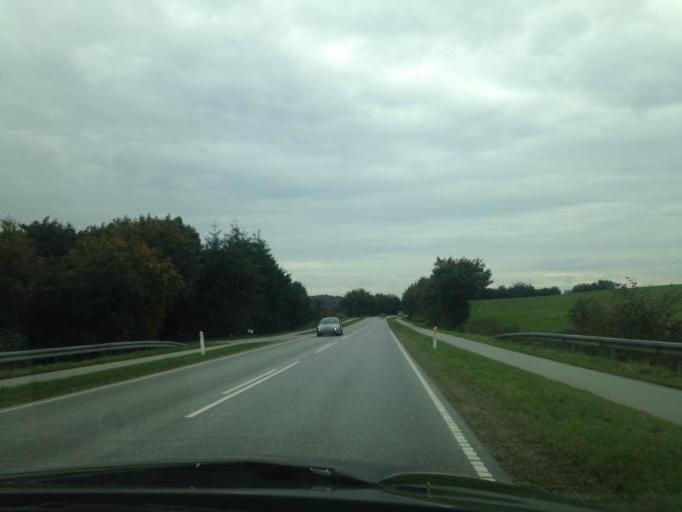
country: DK
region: South Denmark
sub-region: Haderslev Kommune
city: Haderslev
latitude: 55.2465
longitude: 9.4254
